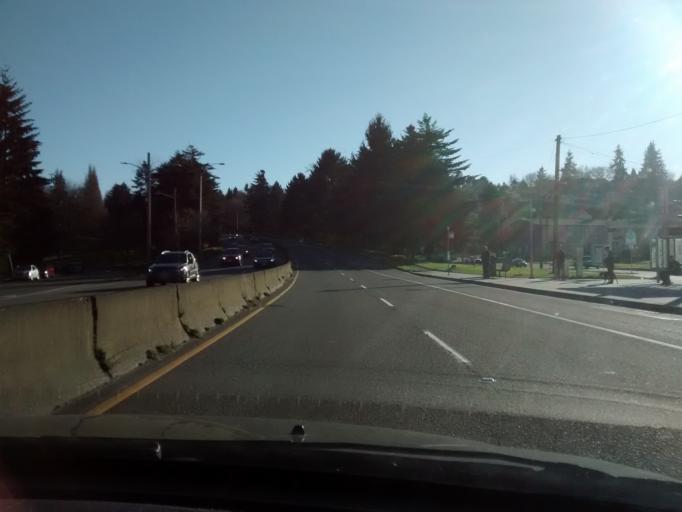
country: US
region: Washington
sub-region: King County
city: Seattle
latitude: 47.6764
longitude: -122.3467
